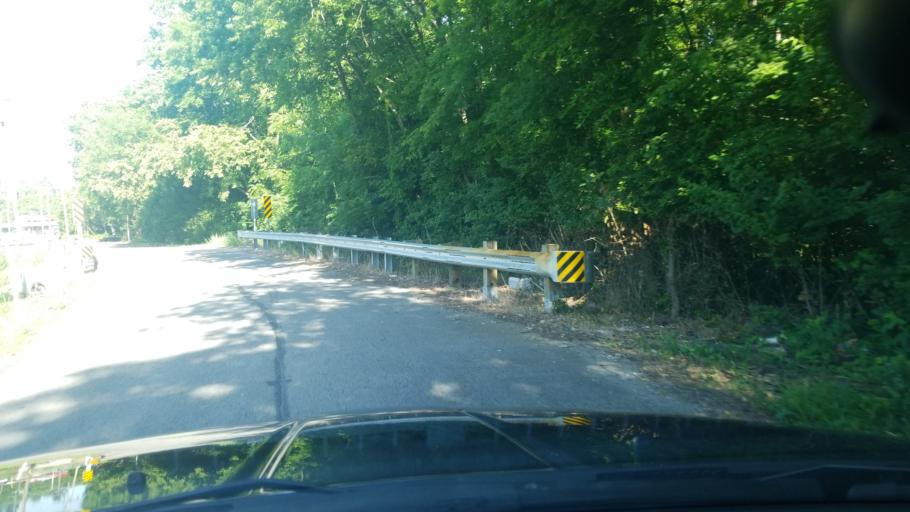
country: US
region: Tennessee
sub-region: Davidson County
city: Nashville
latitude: 36.2331
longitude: -86.7791
